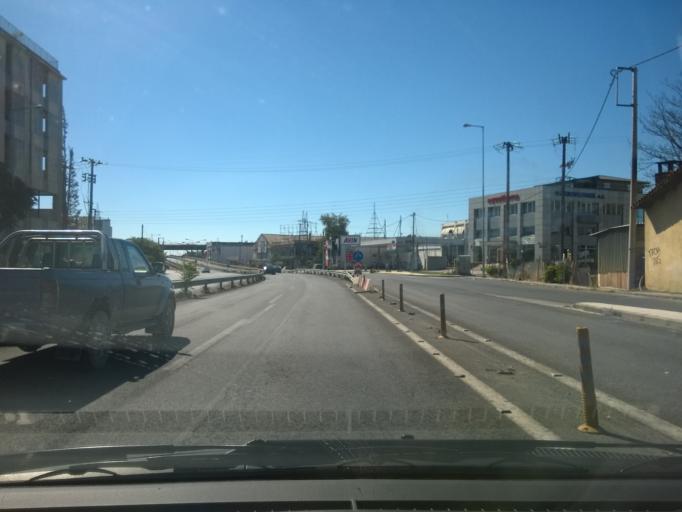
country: GR
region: Central Macedonia
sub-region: Nomos Thessalonikis
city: Stavroupoli
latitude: 40.6798
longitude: 22.9390
